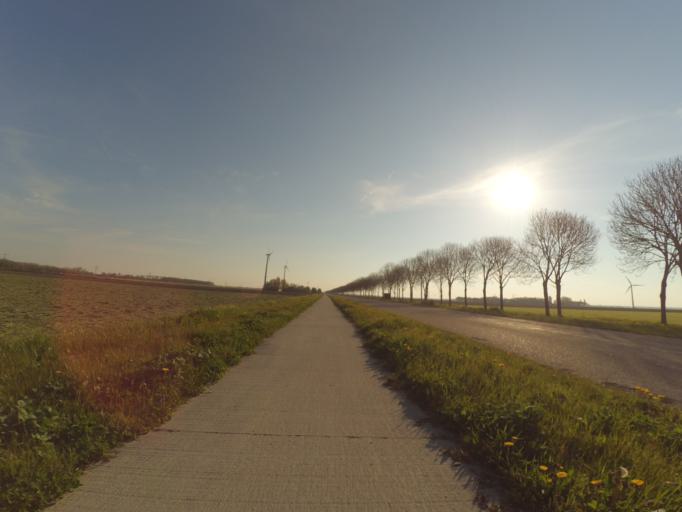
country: NL
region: Utrecht
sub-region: Gemeente Bunschoten
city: Spakenburg
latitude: 52.3989
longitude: 5.3619
